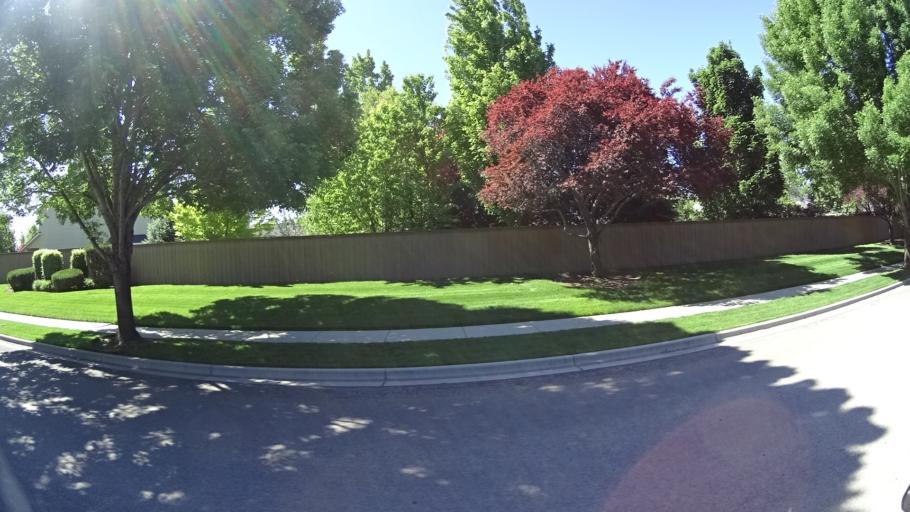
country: US
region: Idaho
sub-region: Ada County
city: Meridian
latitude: 43.6373
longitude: -116.3919
